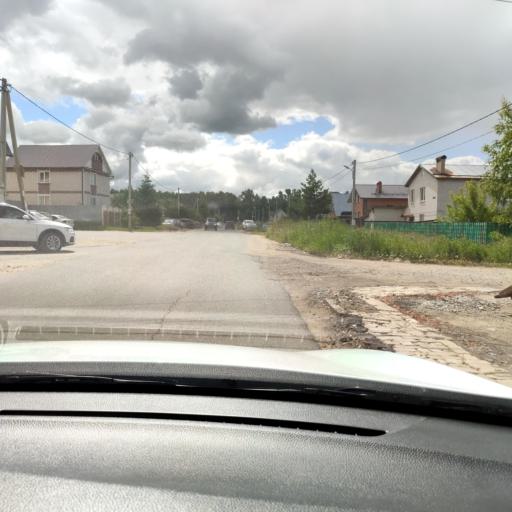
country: RU
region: Tatarstan
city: Vysokaya Gora
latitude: 55.7820
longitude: 49.2636
